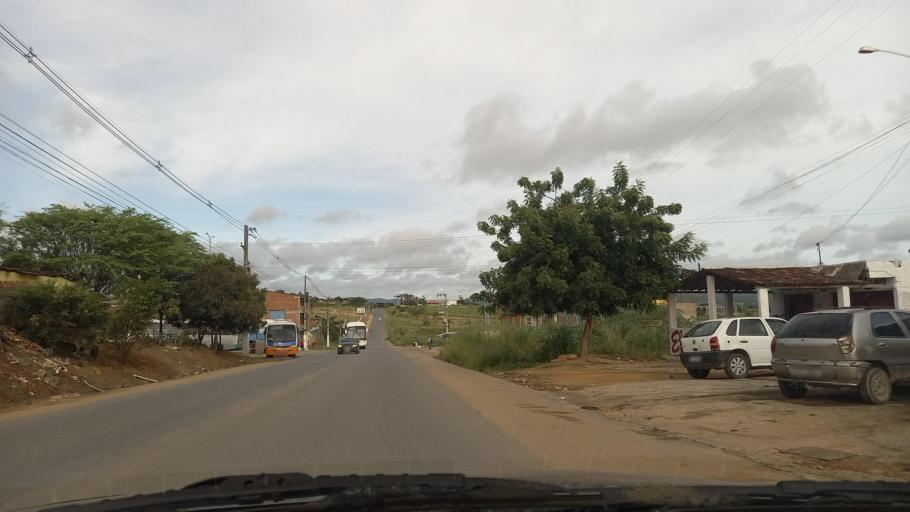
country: BR
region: Pernambuco
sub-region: Vitoria De Santo Antao
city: Vitoria de Santo Antao
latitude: -8.1231
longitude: -35.3353
